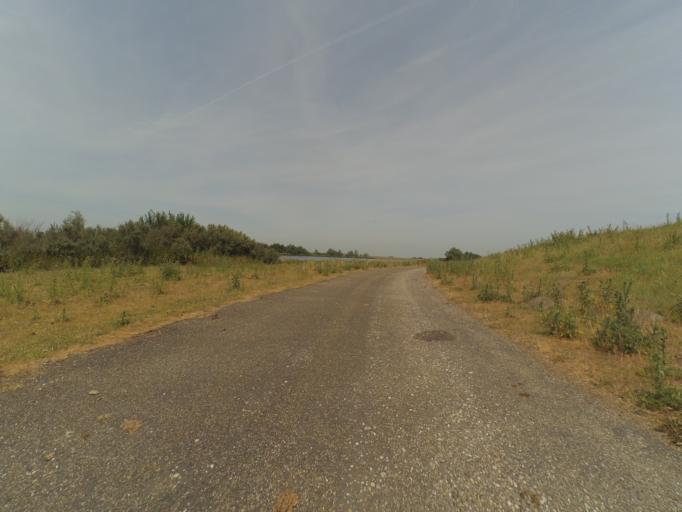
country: NL
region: North Brabant
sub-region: Gemeente Steenbergen
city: Nieuw-Vossemeer
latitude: 51.6001
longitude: 4.1925
